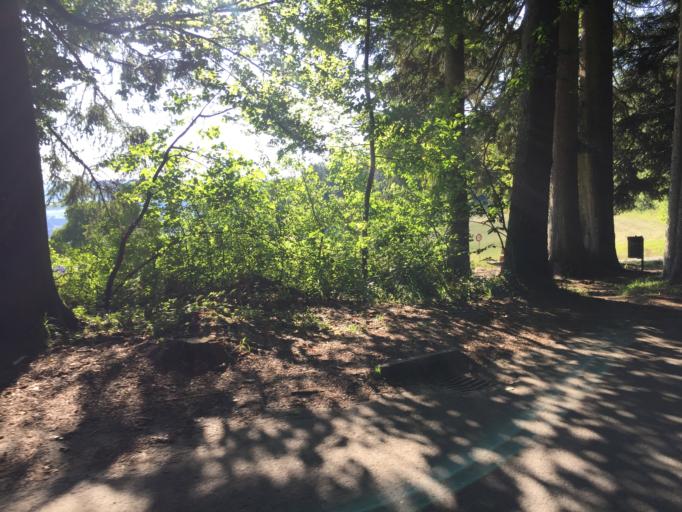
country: CH
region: Lucerne
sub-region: Entlebuch District
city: Oberdiessbach
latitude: 46.8442
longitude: 7.6002
